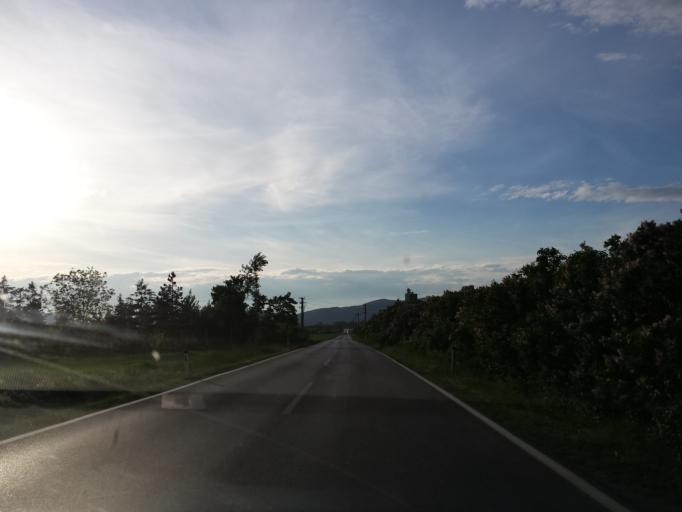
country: AT
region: Lower Austria
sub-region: Politischer Bezirk Baden
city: Oberwaltersdorf
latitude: 47.9889
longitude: 16.3027
